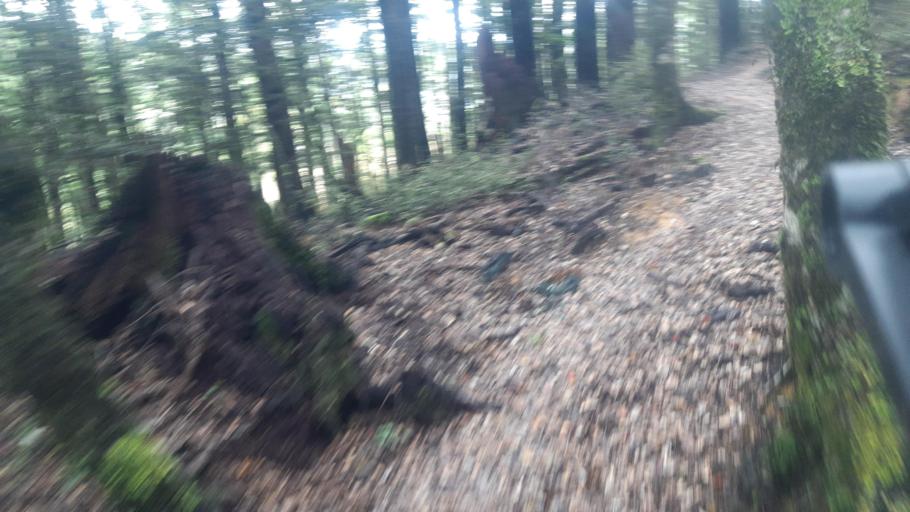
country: NZ
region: Tasman
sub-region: Tasman District
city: Wakefield
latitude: -41.7687
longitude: 172.8177
